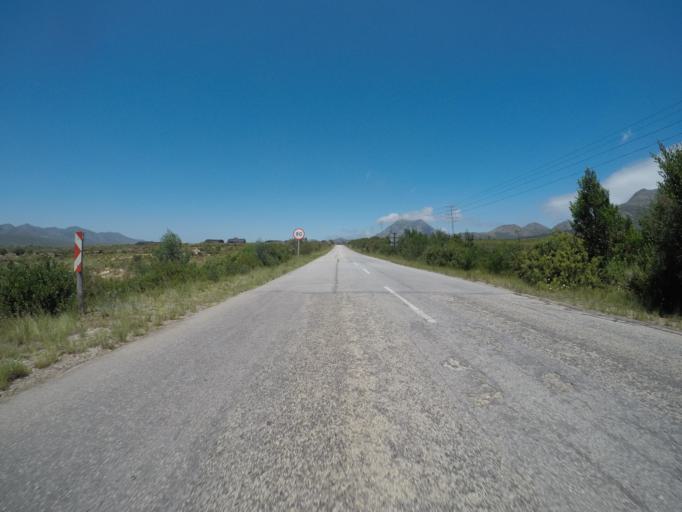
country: ZA
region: Eastern Cape
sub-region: Cacadu District Municipality
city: Kareedouw
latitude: -33.9446
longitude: 24.2720
